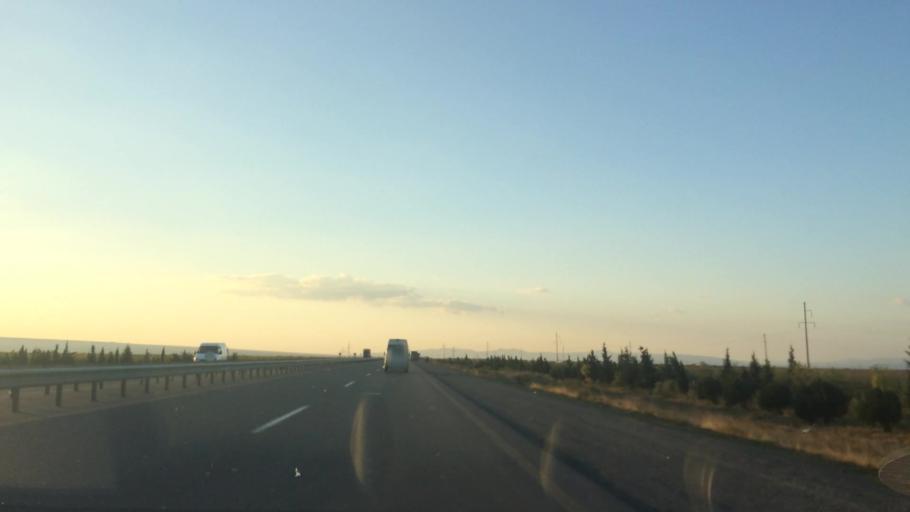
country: AZ
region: Baki
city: Qobustan
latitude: 39.9923
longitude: 49.1937
